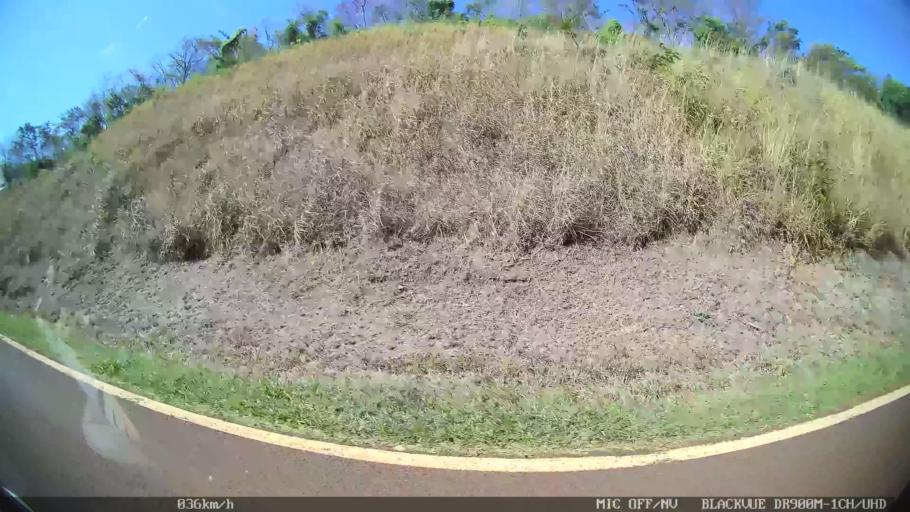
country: BR
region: Sao Paulo
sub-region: Franca
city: Franca
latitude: -20.6331
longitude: -47.4678
